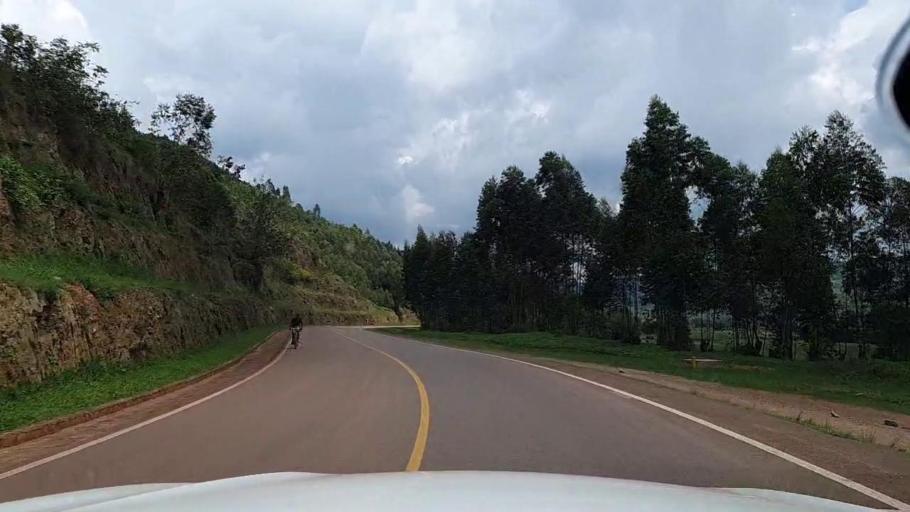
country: RW
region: Kigali
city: Kigali
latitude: -1.8154
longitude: 30.1187
